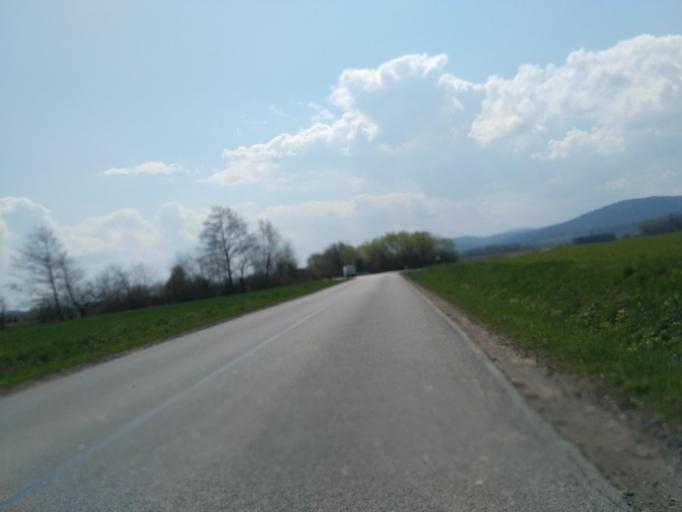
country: PL
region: Subcarpathian Voivodeship
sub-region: Powiat krosnienski
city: Sieniawa
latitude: 49.5327
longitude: 21.9733
